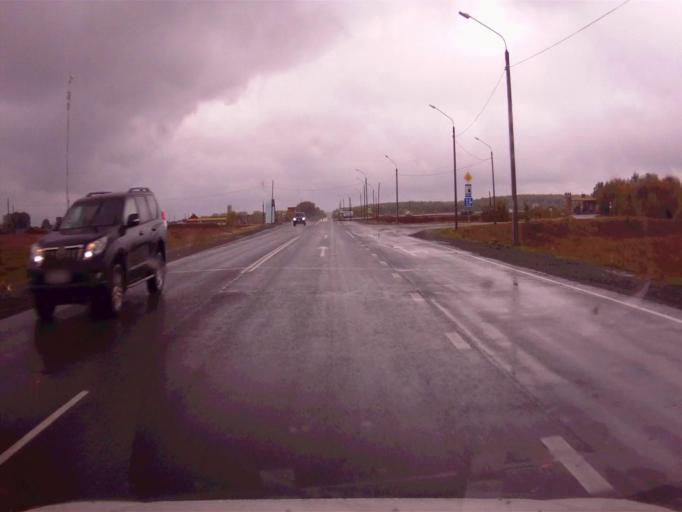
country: RU
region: Chelyabinsk
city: Tayginka
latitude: 55.4983
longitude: 60.6405
